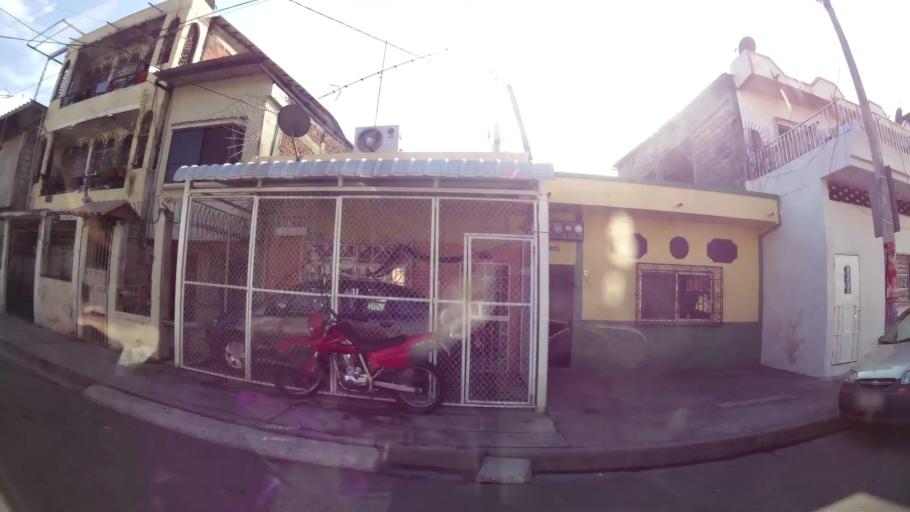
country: EC
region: Guayas
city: Guayaquil
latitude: -2.2037
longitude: -79.9226
